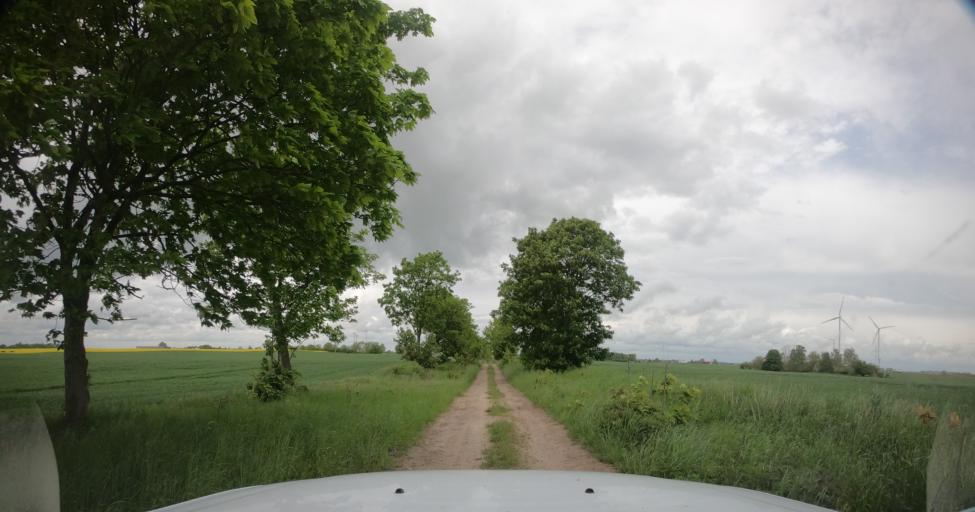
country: PL
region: West Pomeranian Voivodeship
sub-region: Powiat pyrzycki
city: Kozielice
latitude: 53.0865
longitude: 14.8244
